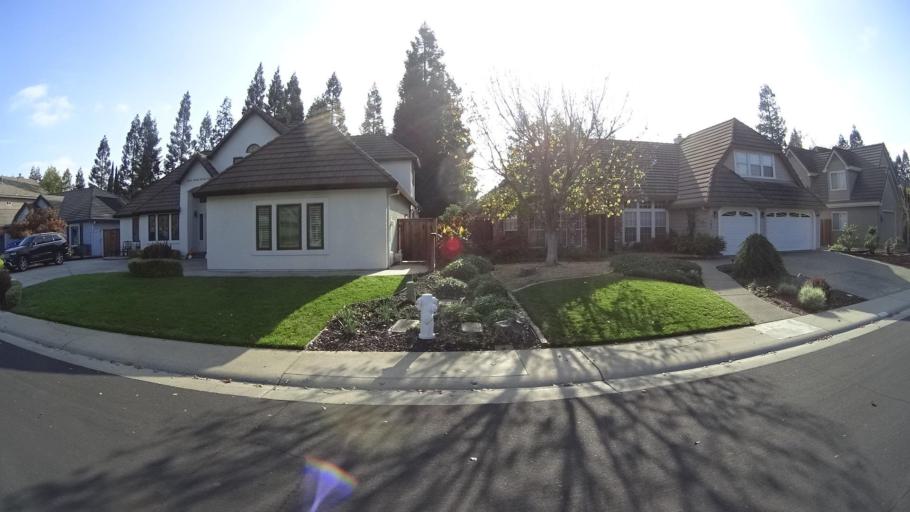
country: US
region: California
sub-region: Sacramento County
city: Elk Grove
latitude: 38.4157
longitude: -121.3564
